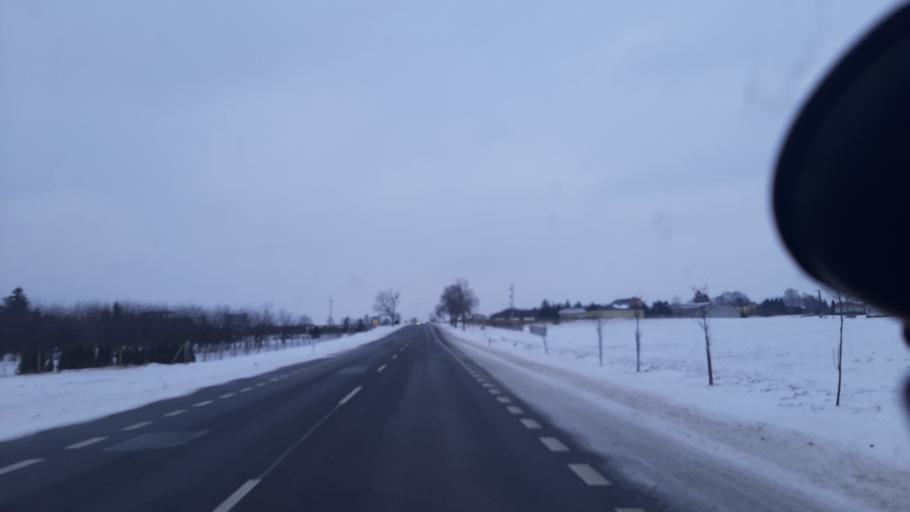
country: PL
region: Lublin Voivodeship
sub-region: Powiat pulawski
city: Kurow
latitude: 51.3836
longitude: 22.2202
